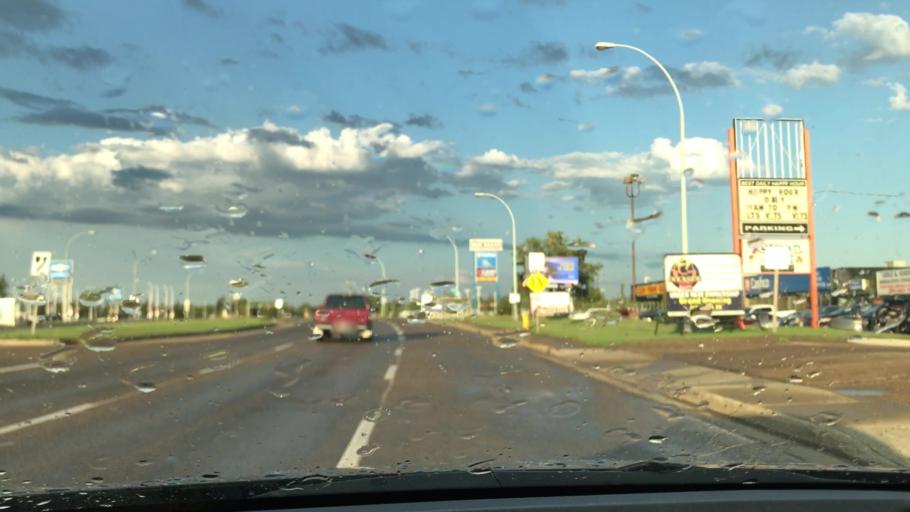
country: CA
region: Alberta
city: Edmonton
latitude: 53.4653
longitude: -113.4719
